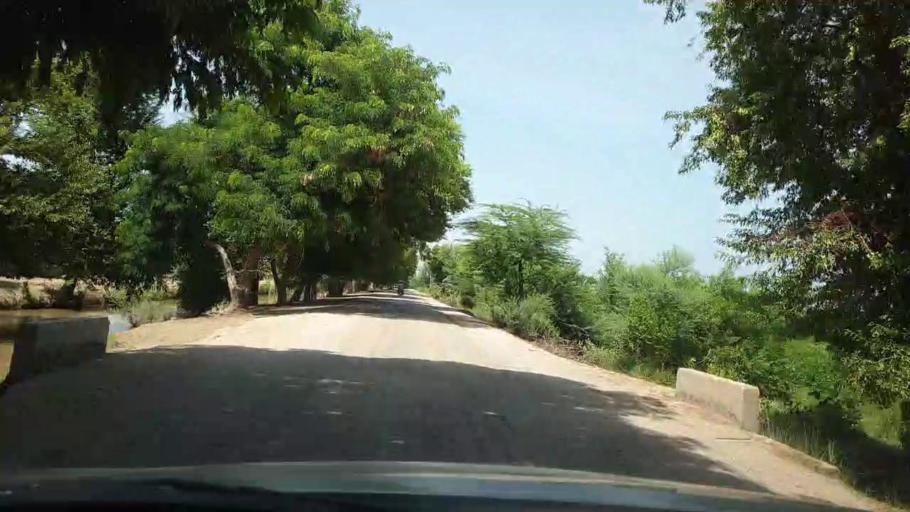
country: PK
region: Sindh
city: Pano Aqil
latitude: 27.6982
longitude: 69.1116
